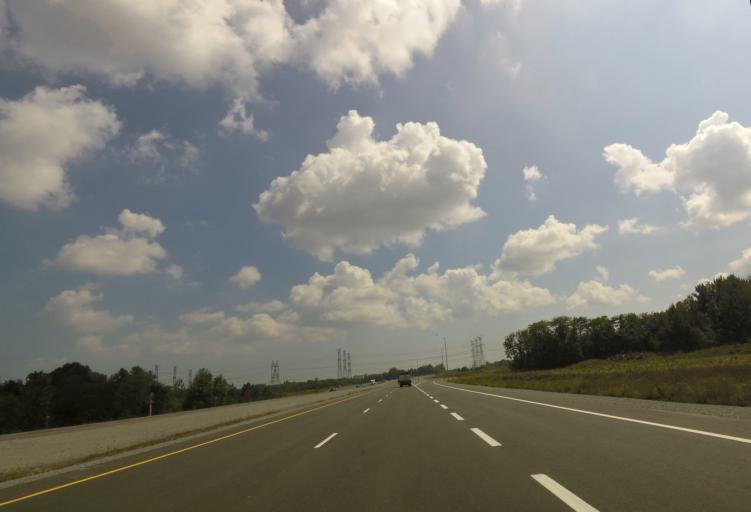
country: CA
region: Ontario
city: Ajax
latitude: 43.9267
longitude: -79.0004
